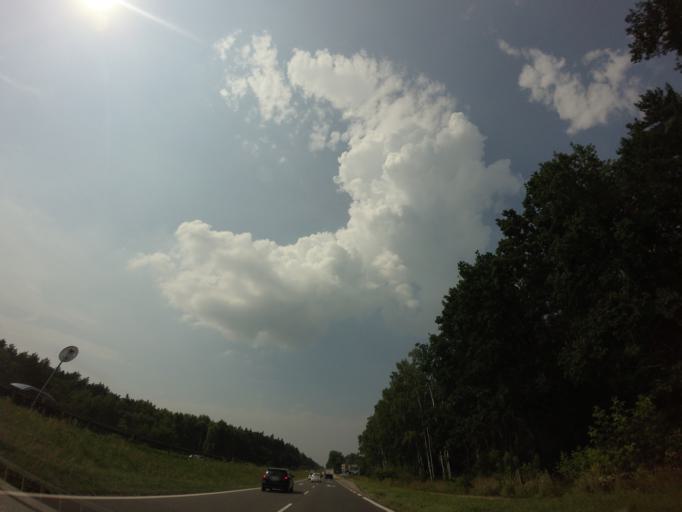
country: PL
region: West Pomeranian Voivodeship
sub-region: Powiat gryfinski
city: Stare Czarnowo
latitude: 53.3656
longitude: 14.7307
